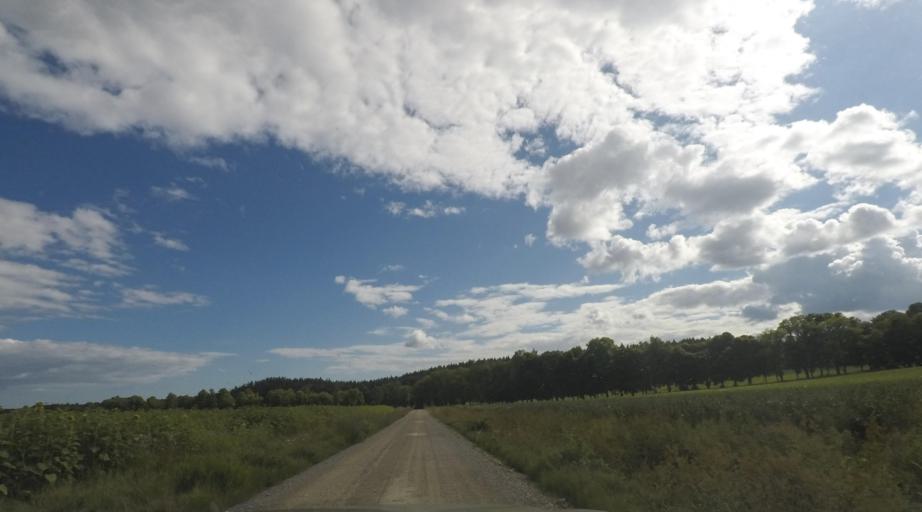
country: SE
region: Stockholm
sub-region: Sodertalje Kommun
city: Pershagen
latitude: 59.1106
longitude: 17.6681
